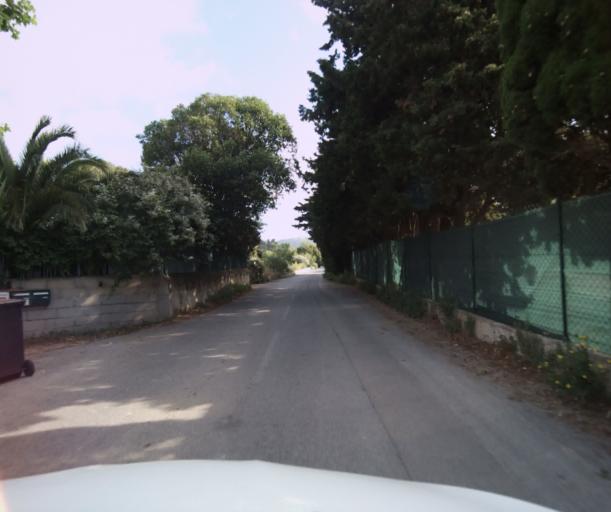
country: FR
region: Provence-Alpes-Cote d'Azur
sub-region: Departement du Var
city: Ollioules
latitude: 43.1242
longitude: 5.8426
